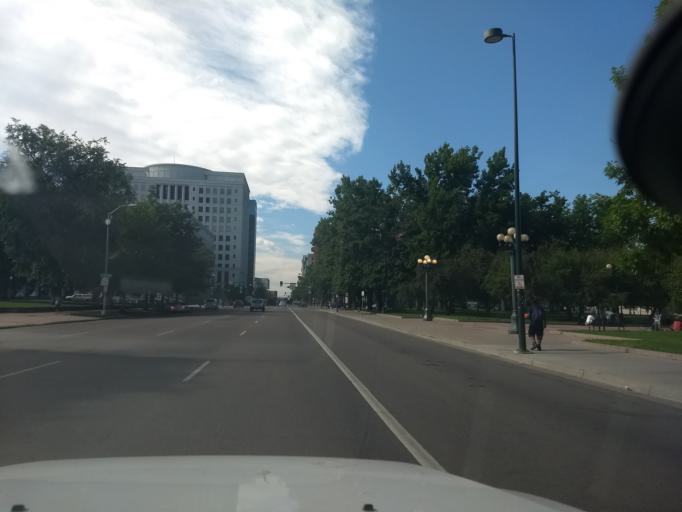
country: US
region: Colorado
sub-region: Denver County
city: Denver
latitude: 39.7396
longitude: -104.9874
